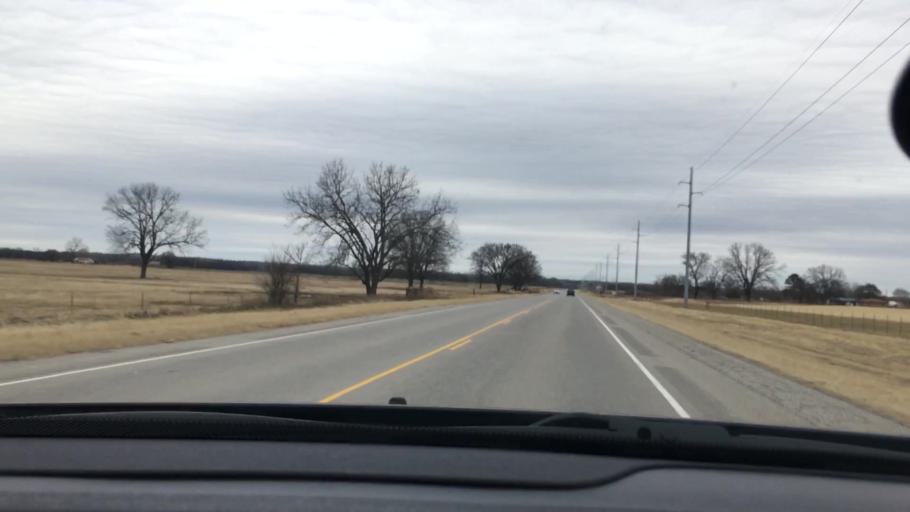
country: US
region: Oklahoma
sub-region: Marshall County
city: Oakland
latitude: 34.1968
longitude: -96.8022
